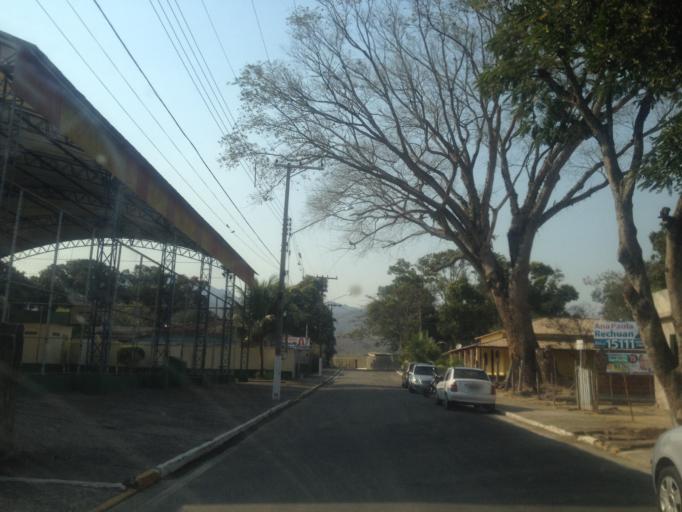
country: BR
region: Rio de Janeiro
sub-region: Porto Real
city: Porto Real
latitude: -22.4644
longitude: -44.3564
